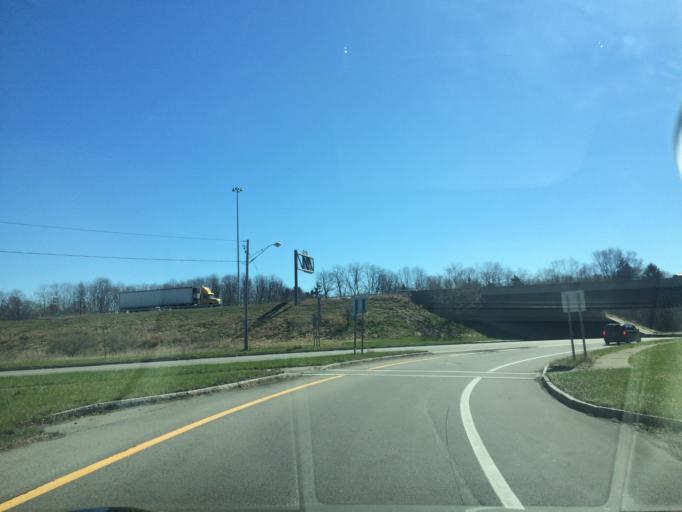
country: US
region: New York
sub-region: Monroe County
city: East Rochester
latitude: 43.1112
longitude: -77.5084
